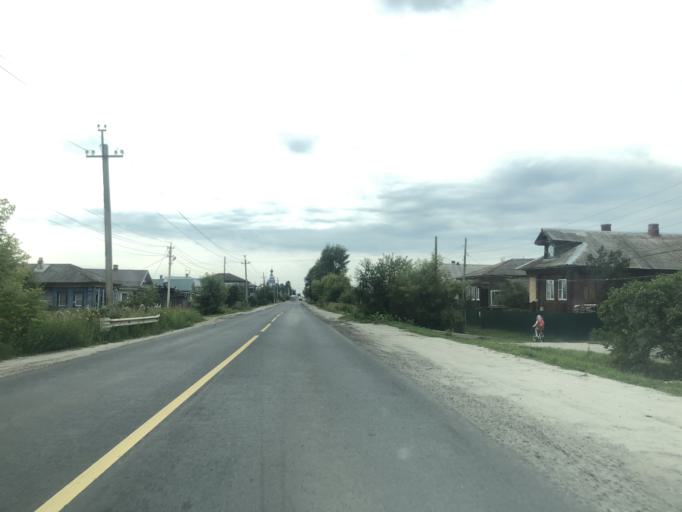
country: RU
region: Ivanovo
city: Pestyaki
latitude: 56.7056
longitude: 42.6772
